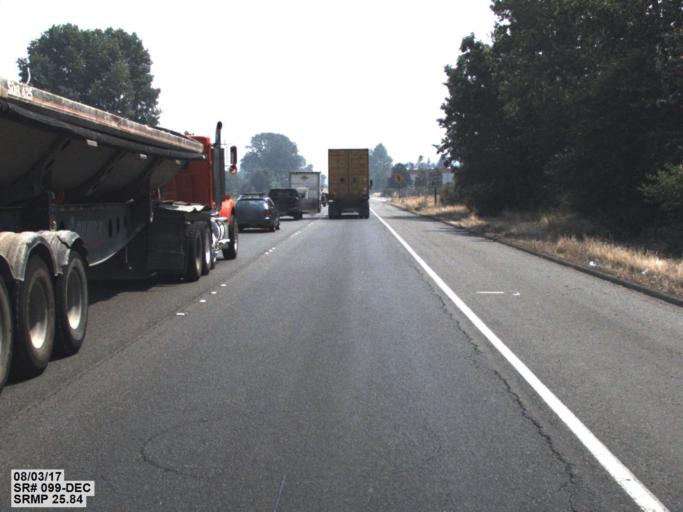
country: US
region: Washington
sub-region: King County
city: White Center
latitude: 47.5318
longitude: -122.3299
